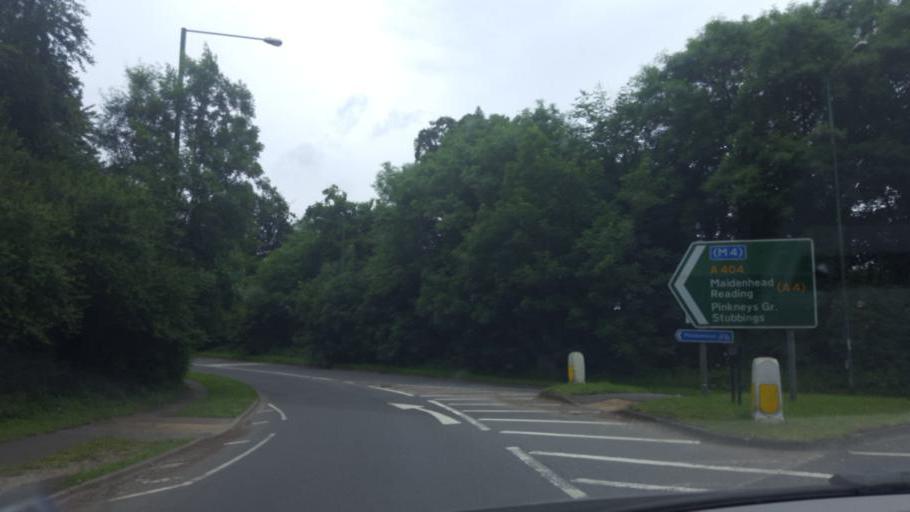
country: GB
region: England
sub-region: Royal Borough of Windsor and Maidenhead
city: Hurley
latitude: 51.5318
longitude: -0.7874
